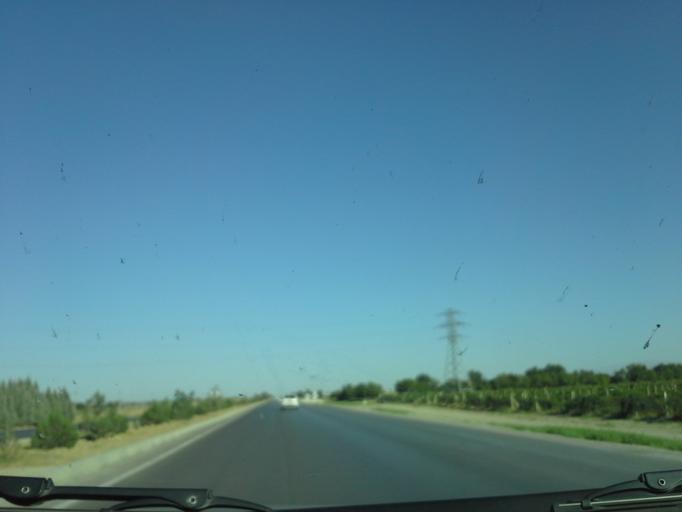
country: TM
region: Ahal
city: Abadan
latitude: 38.0845
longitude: 58.1199
